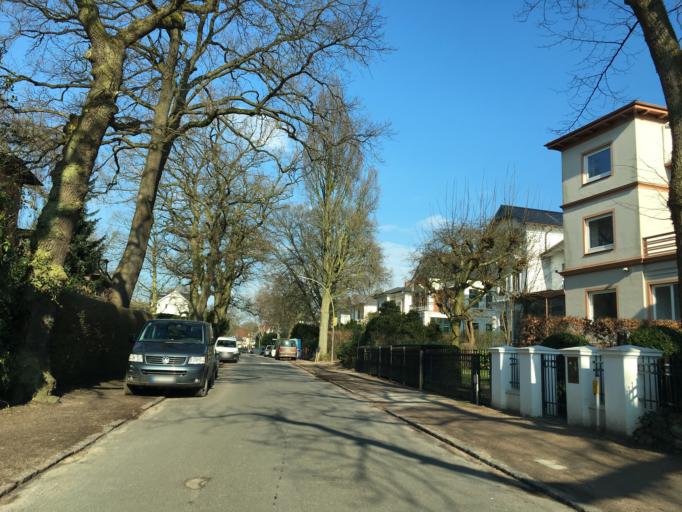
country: DE
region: Hamburg
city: Eidelstedt
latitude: 53.5598
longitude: 9.8781
